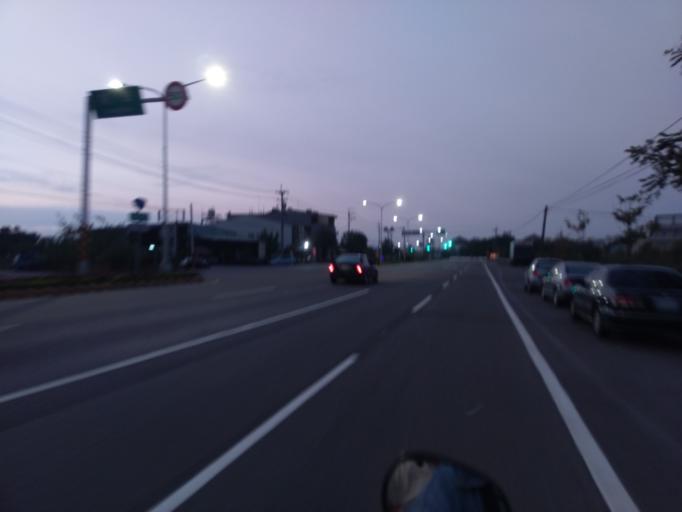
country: TW
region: Taiwan
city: Xinying
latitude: 23.1931
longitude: 120.3245
